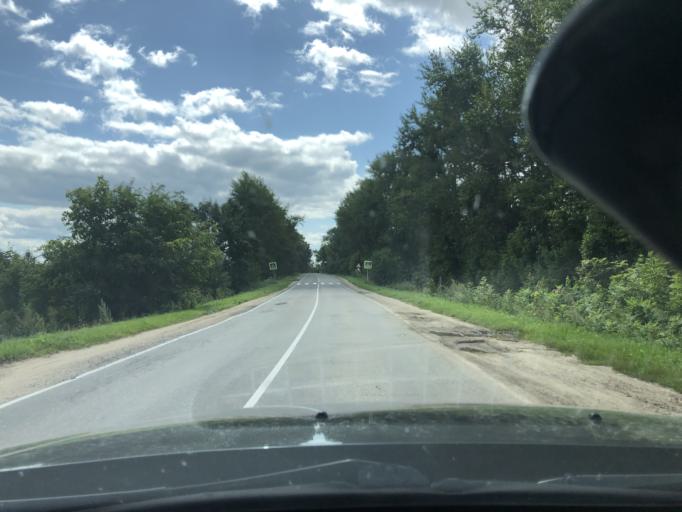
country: RU
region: Tula
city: Revyakino
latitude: 54.3578
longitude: 37.6359
